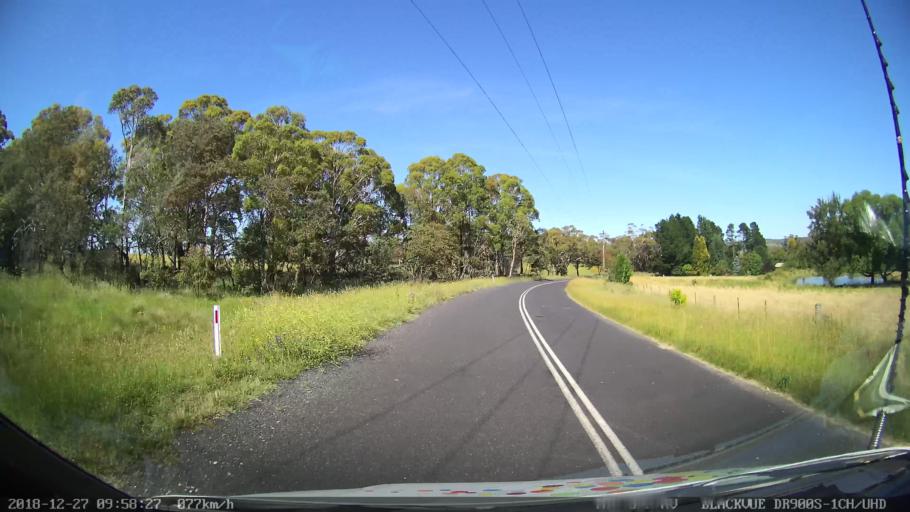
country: AU
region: New South Wales
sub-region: Lithgow
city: Portland
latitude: -33.4303
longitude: 149.9640
